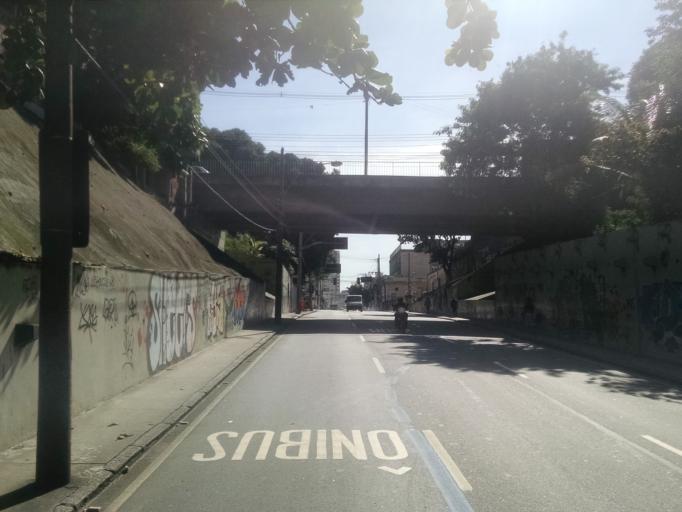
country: BR
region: Rio de Janeiro
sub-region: Rio De Janeiro
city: Rio de Janeiro
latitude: -22.9042
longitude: -43.2784
